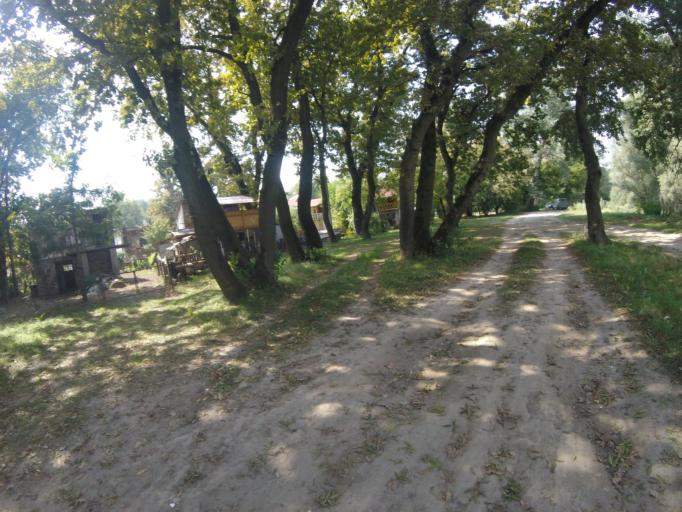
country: HU
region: Bacs-Kiskun
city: Baja
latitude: 46.1969
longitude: 18.9204
